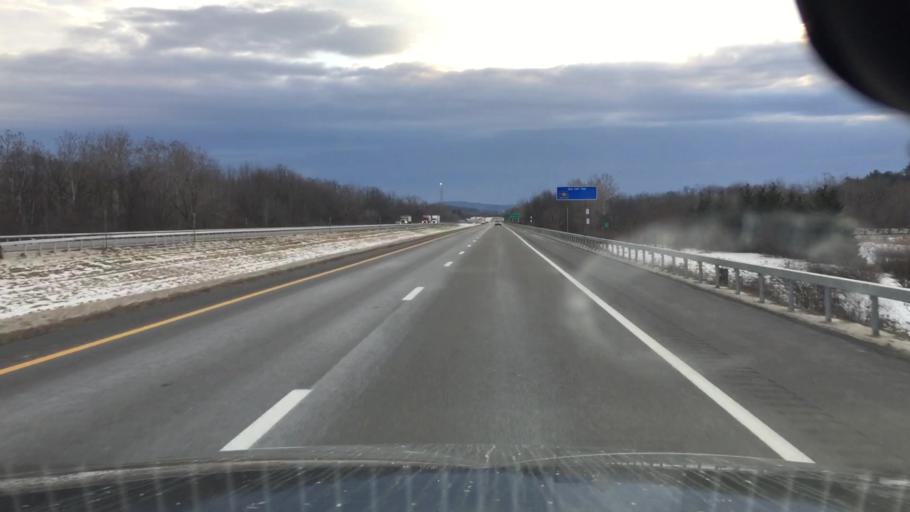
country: US
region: Pennsylvania
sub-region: Bradford County
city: South Waverly
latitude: 42.0009
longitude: -76.6024
